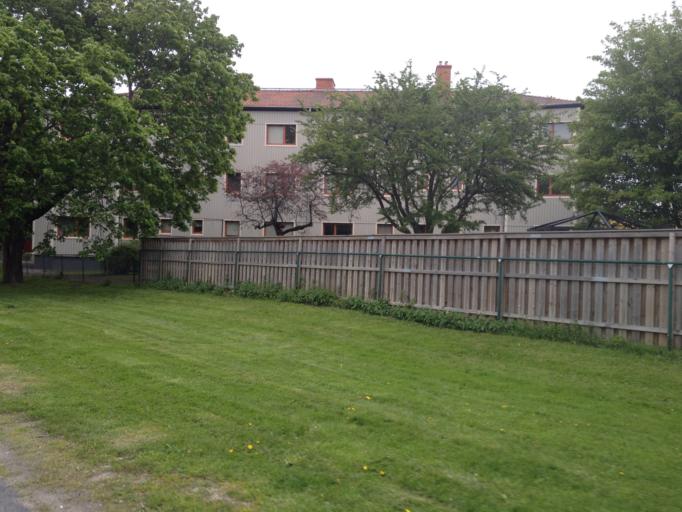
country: SE
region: OEstergoetland
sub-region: Norrkopings Kommun
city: Norrkoping
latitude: 58.5964
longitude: 16.1601
